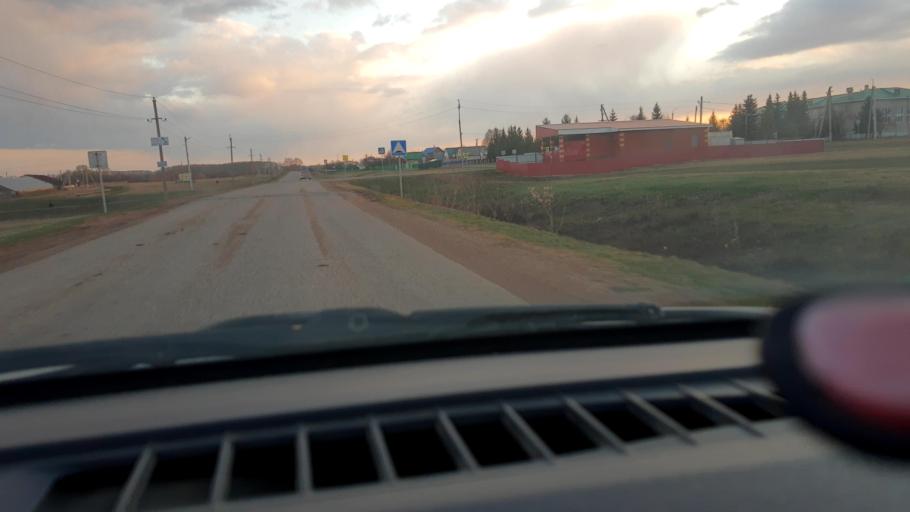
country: RU
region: Bashkortostan
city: Asanovo
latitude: 54.9071
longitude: 55.4965
